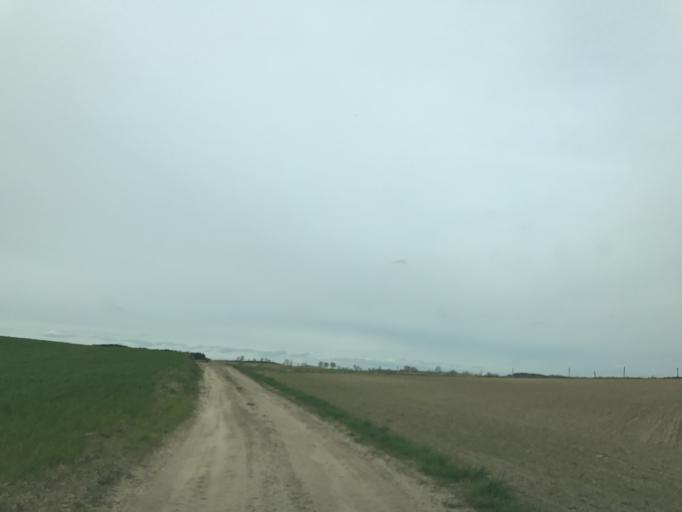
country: PL
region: Warmian-Masurian Voivodeship
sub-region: Powiat ilawski
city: Lubawa
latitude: 53.4340
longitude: 19.8145
